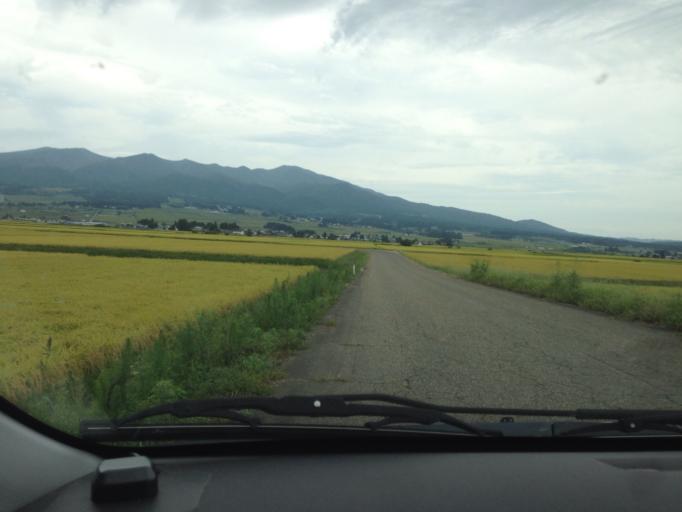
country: JP
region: Fukushima
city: Kitakata
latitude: 37.6314
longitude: 139.8966
